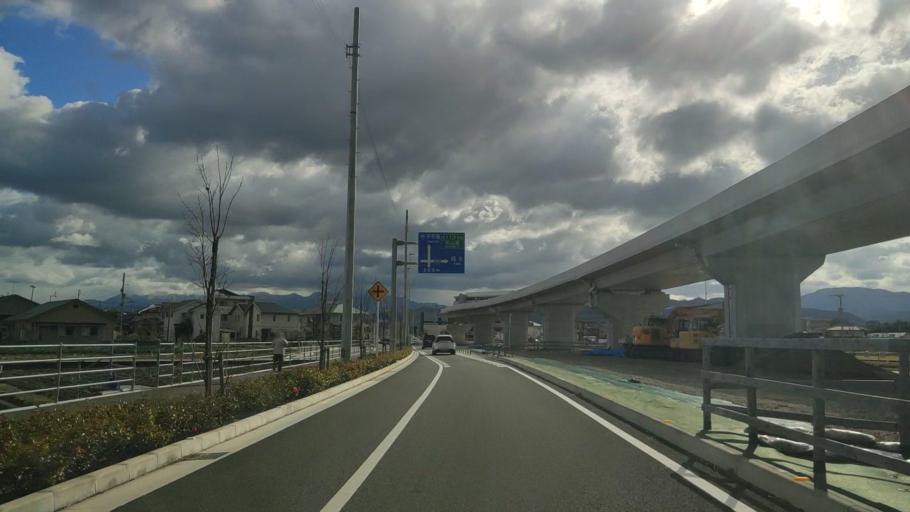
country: JP
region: Ehime
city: Masaki-cho
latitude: 33.8129
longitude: 132.7222
